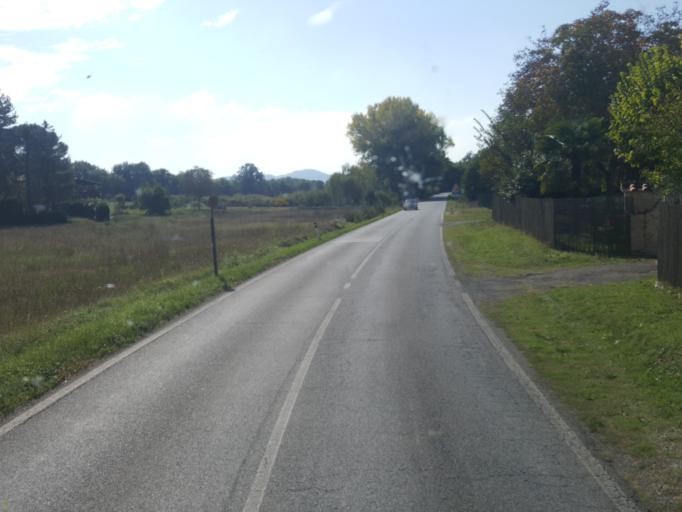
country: IT
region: Tuscany
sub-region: Provincia di Siena
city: Colle di Val d'Elsa
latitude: 43.3859
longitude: 11.0861
